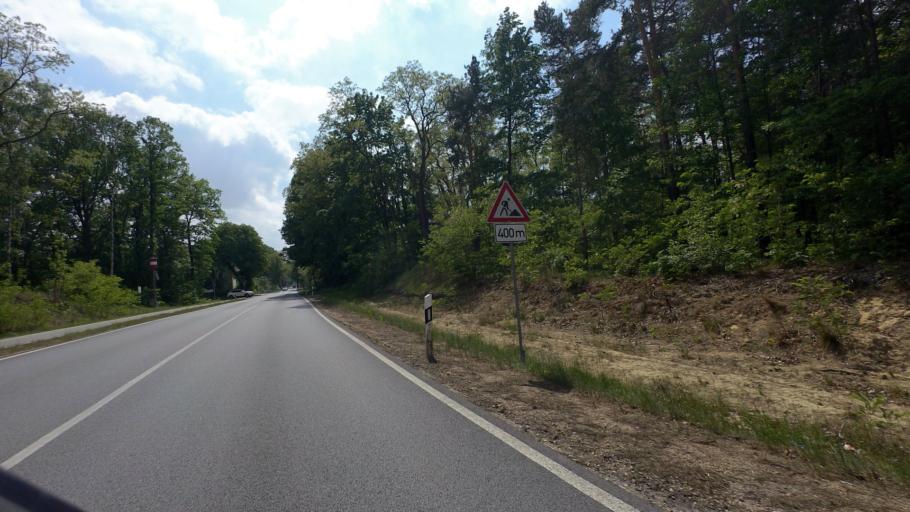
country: DE
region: Saxony
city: Rietschen
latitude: 51.4142
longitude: 14.7885
